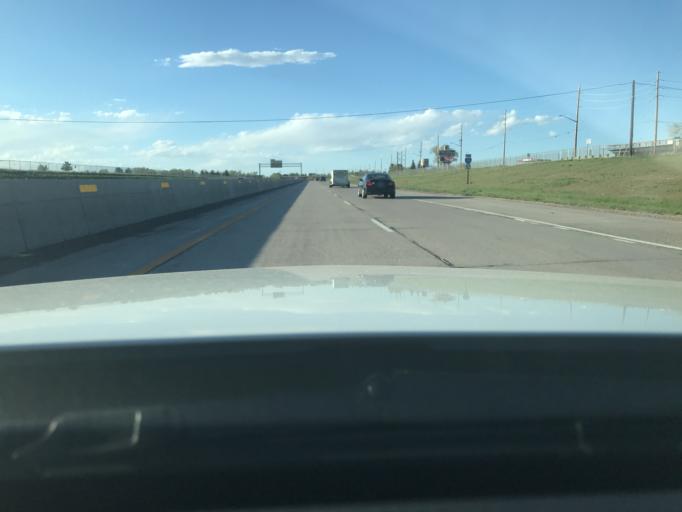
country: US
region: Wyoming
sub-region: Laramie County
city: Cheyenne
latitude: 41.1523
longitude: -104.8389
